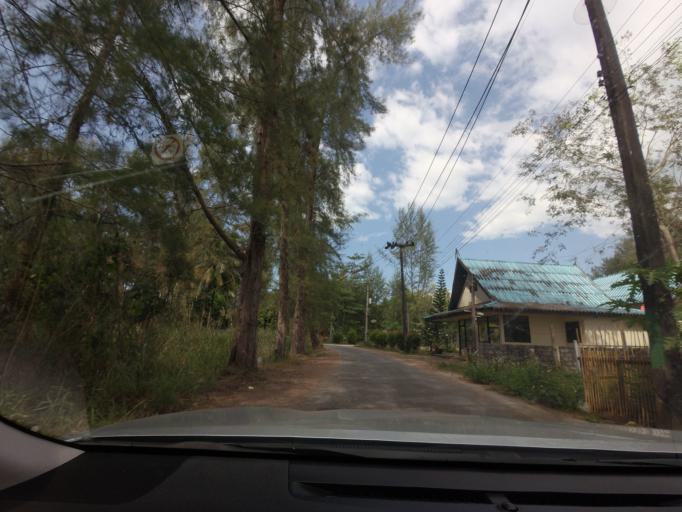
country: TH
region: Phangnga
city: Ban Khao Lak
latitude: 8.7331
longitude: 98.2427
